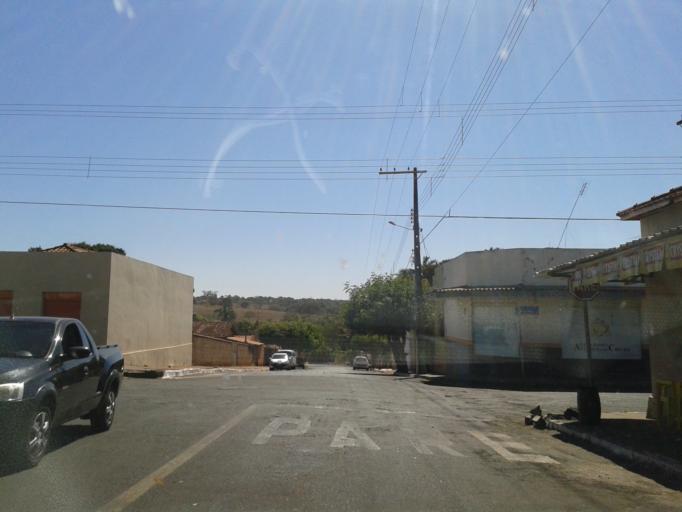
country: BR
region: Minas Gerais
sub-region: Santa Vitoria
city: Santa Vitoria
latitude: -18.8389
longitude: -50.1252
